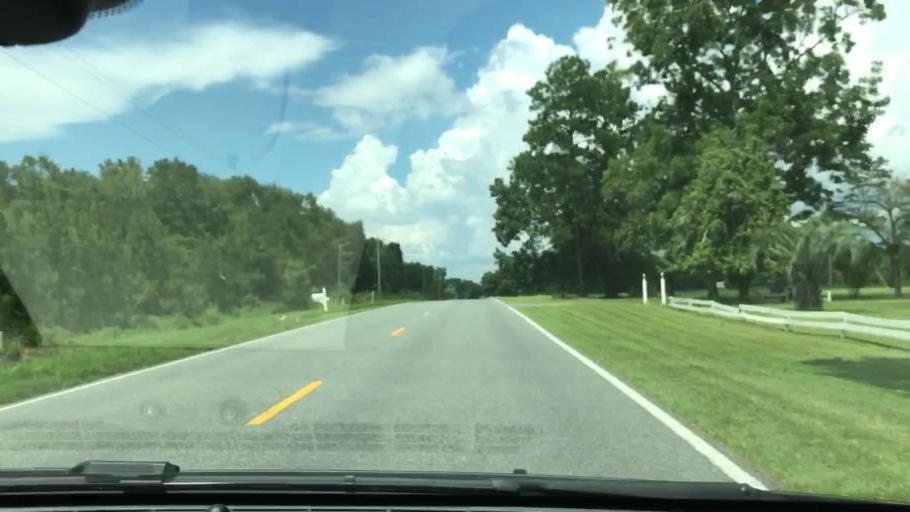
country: US
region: Florida
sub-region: Jackson County
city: Malone
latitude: 30.9511
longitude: -85.1182
